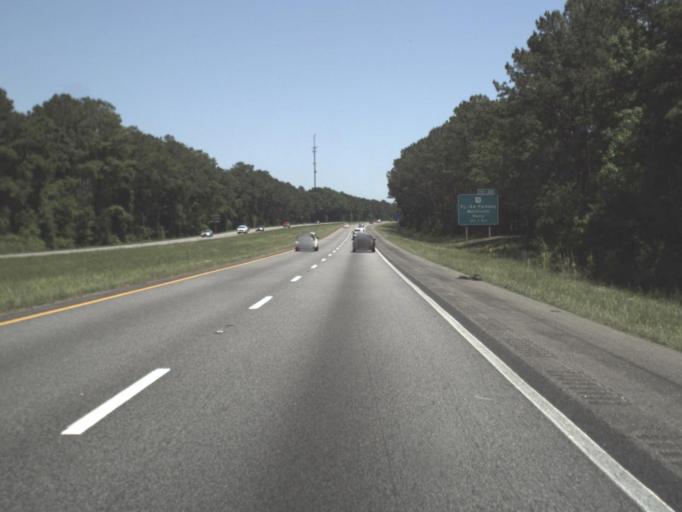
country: US
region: Florida
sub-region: Jefferson County
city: Monticello
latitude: 30.4783
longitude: -83.9117
